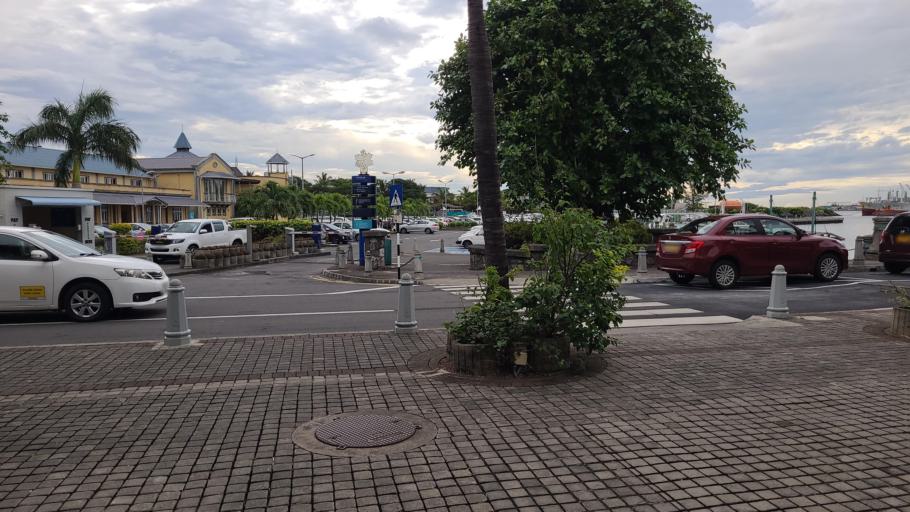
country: MU
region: Port Louis
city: Port Louis
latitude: -20.1608
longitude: 57.4975
